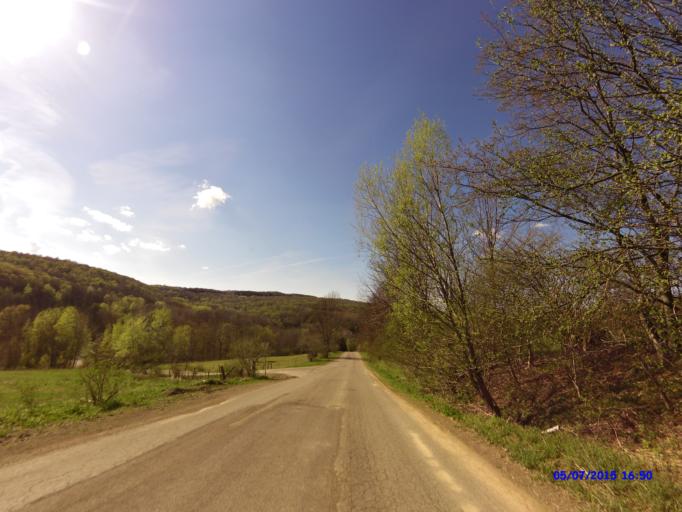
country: US
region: New York
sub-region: Cattaraugus County
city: Little Valley
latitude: 42.2849
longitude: -78.7155
